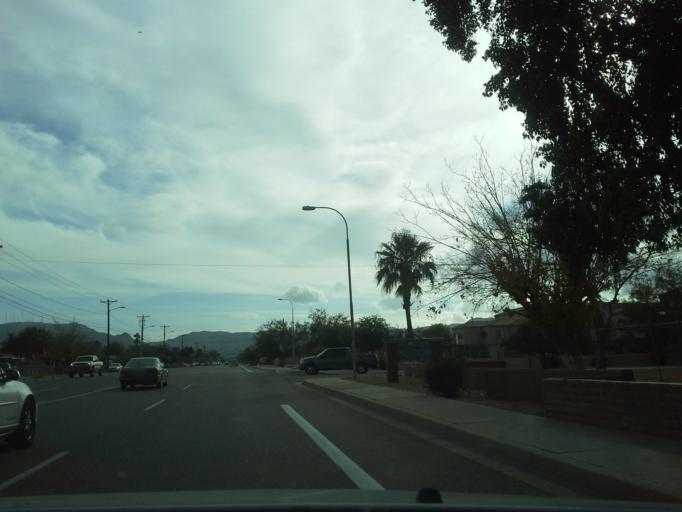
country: US
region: Arizona
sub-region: Maricopa County
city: Phoenix
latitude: 33.3891
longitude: -112.0820
